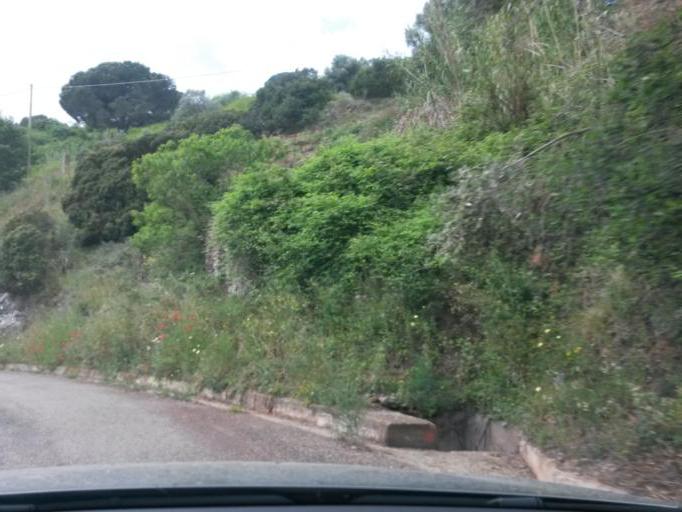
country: IT
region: Tuscany
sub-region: Provincia di Livorno
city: Rio nell'Elba
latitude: 42.8187
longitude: 10.4015
